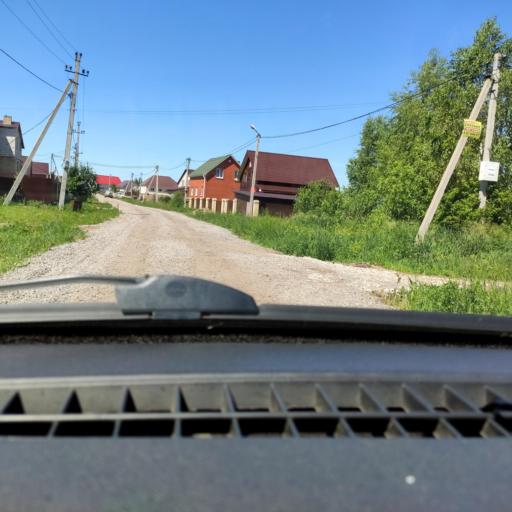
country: RU
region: Bashkortostan
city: Iglino
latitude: 54.7970
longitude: 56.2821
